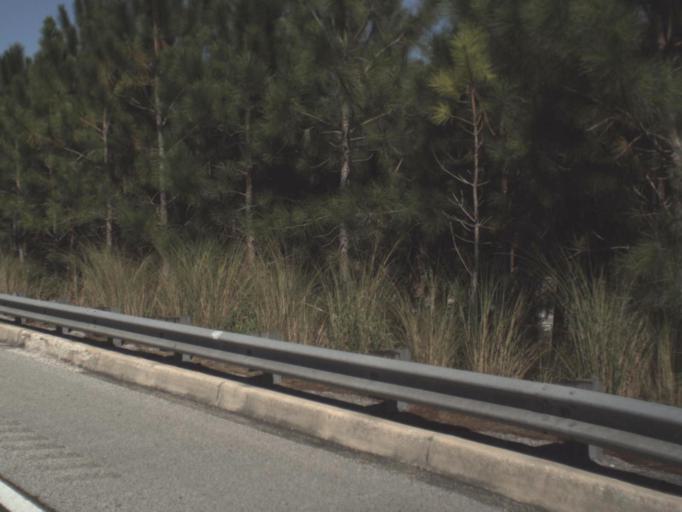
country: US
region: Florida
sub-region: Lake County
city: Yalaha
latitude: 28.6765
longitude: -81.8550
